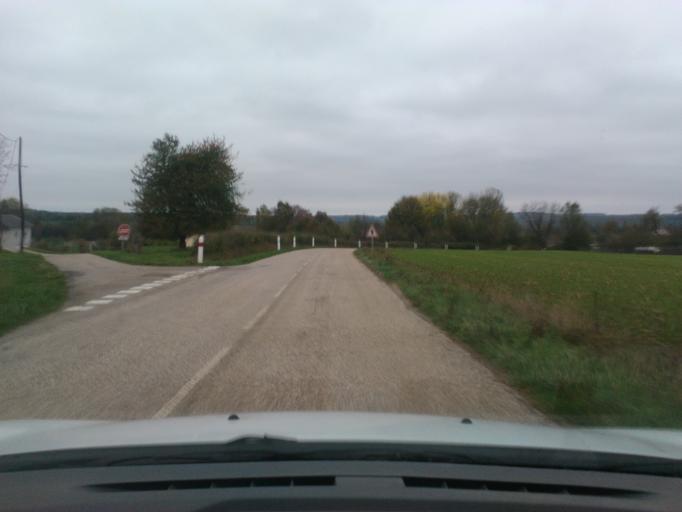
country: FR
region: Lorraine
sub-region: Departement des Vosges
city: Dogneville
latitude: 48.2799
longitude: 6.4803
